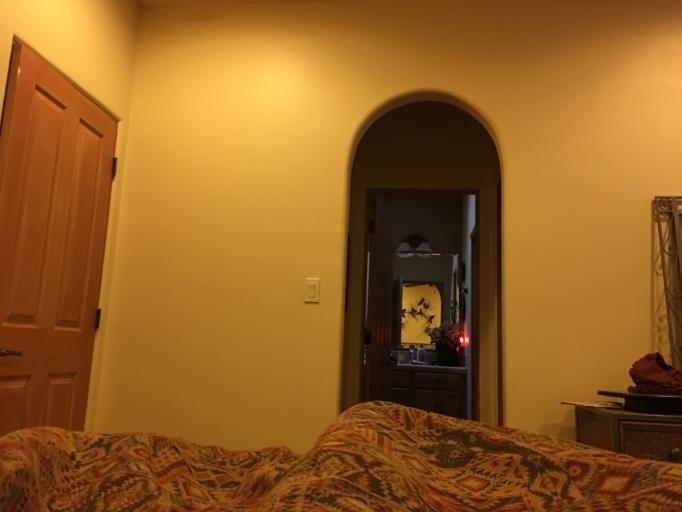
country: US
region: New Mexico
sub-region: Santa Fe County
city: Agua Fria
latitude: 35.6301
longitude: -105.9899
